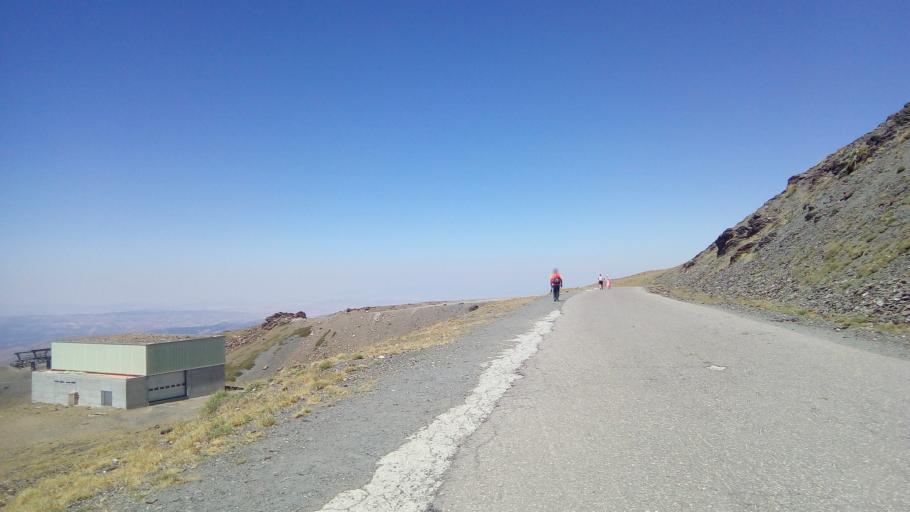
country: ES
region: Andalusia
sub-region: Provincia de Granada
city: Guejar-Sierra
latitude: 37.0820
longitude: -3.3827
